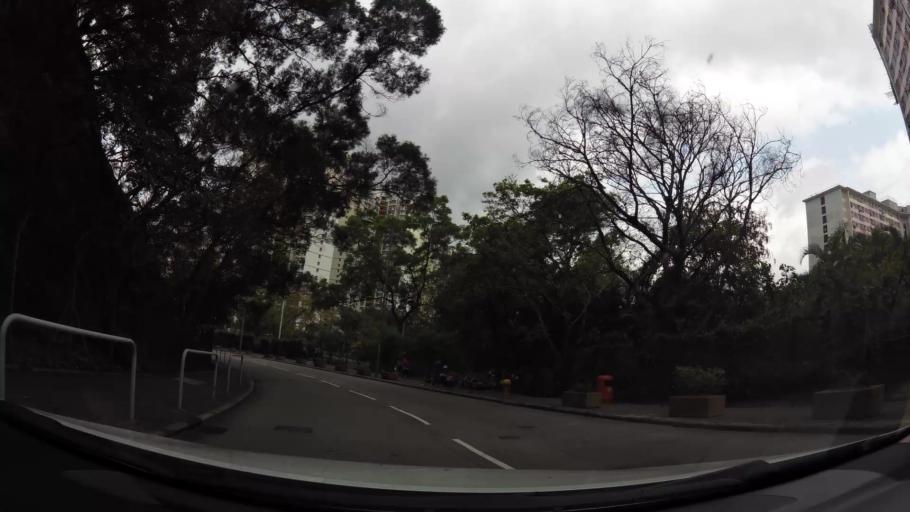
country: HK
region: Kowloon City
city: Kowloon
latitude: 22.3198
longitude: 114.2193
